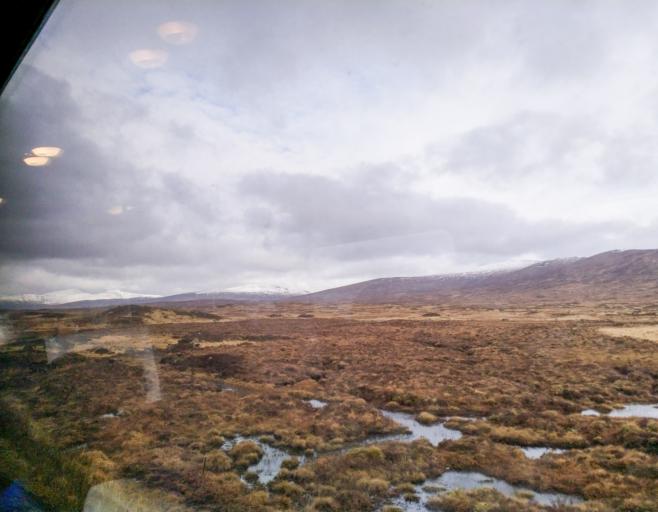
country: GB
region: Scotland
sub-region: Highland
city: Spean Bridge
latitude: 56.7062
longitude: -4.5943
